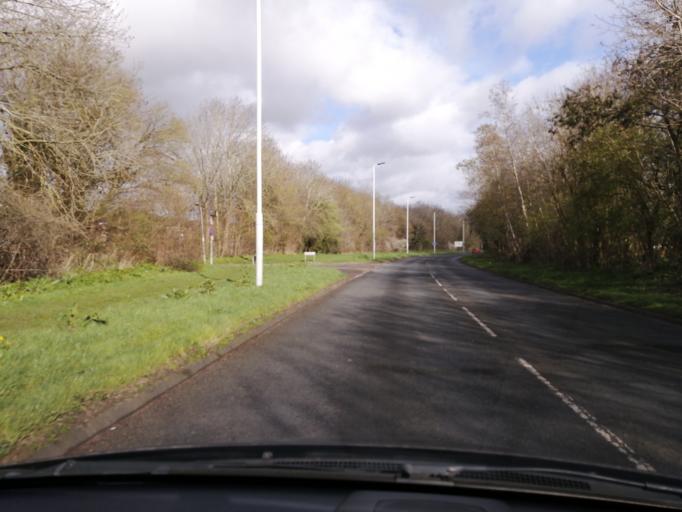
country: GB
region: England
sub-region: Peterborough
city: Marholm
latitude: 52.6010
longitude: -0.2888
